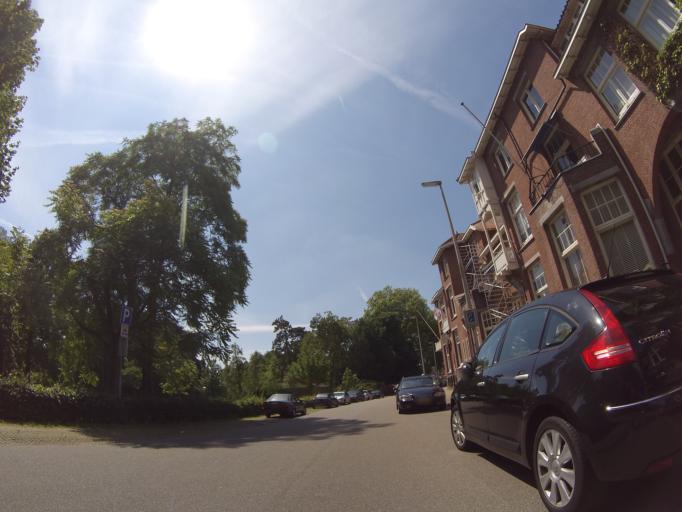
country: NL
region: Utrecht
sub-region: Gemeente Utrecht
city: Utrecht
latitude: 52.0892
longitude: 5.1399
